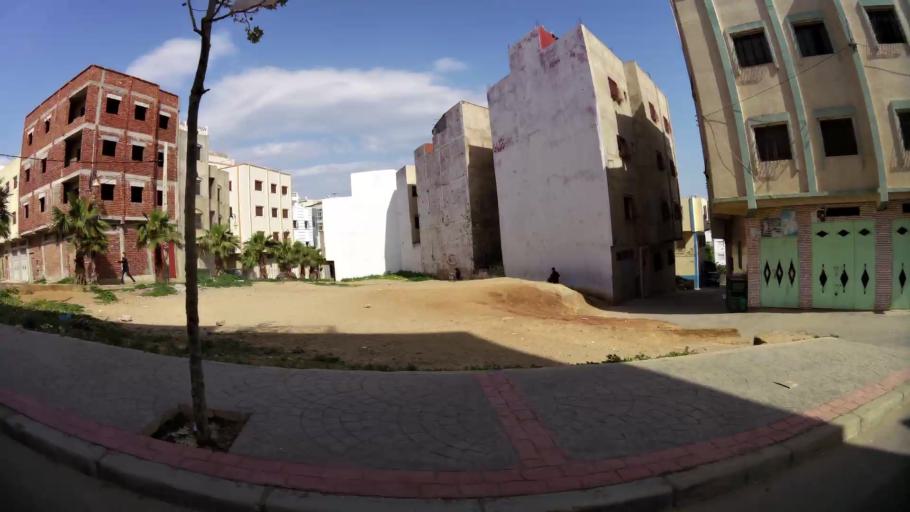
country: MA
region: Tanger-Tetouan
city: Tetouan
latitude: 35.5888
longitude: -5.3585
